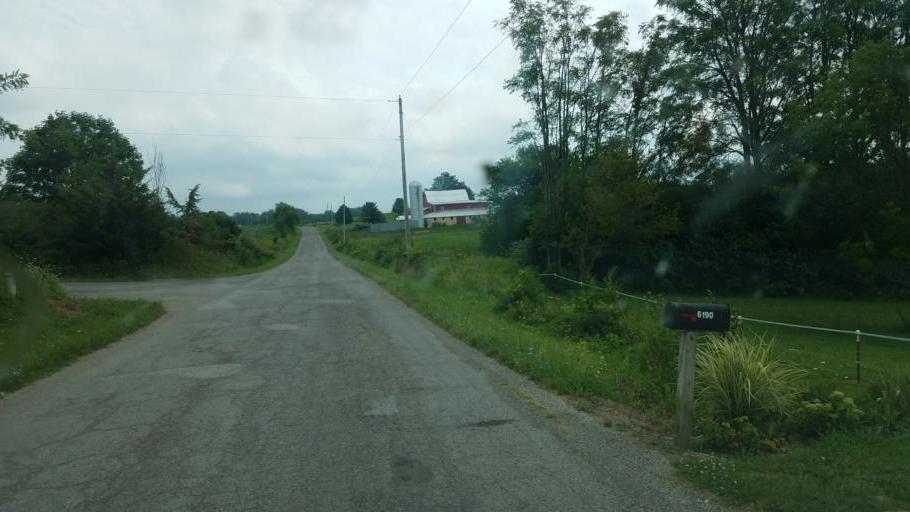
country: US
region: Ohio
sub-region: Morrow County
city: Mount Gilead
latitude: 40.5342
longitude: -82.7211
